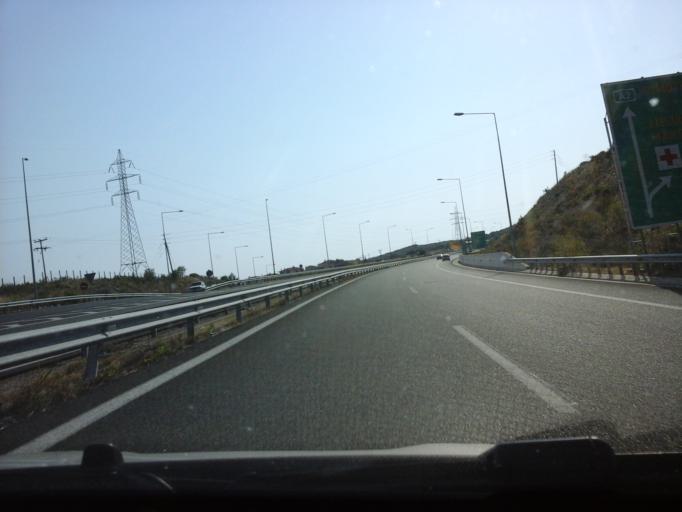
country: GR
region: East Macedonia and Thrace
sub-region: Nomos Evrou
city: Alexandroupoli
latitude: 40.8604
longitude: 25.7557
